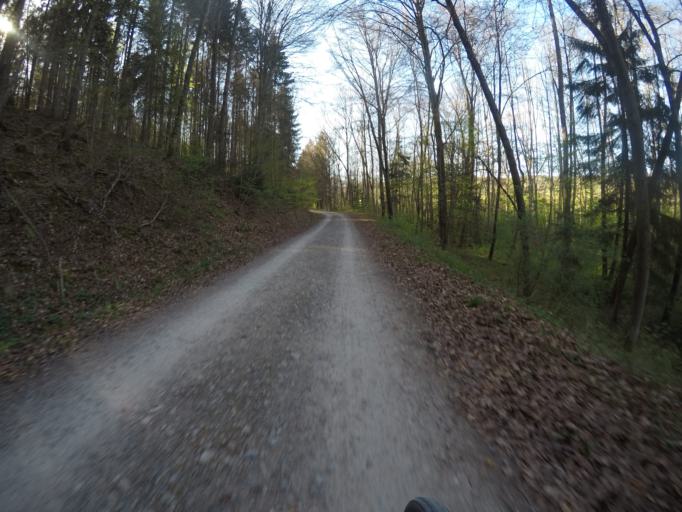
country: DE
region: Baden-Wuerttemberg
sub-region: Regierungsbezirk Stuttgart
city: Schlaitdorf
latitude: 48.6208
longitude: 9.2175
